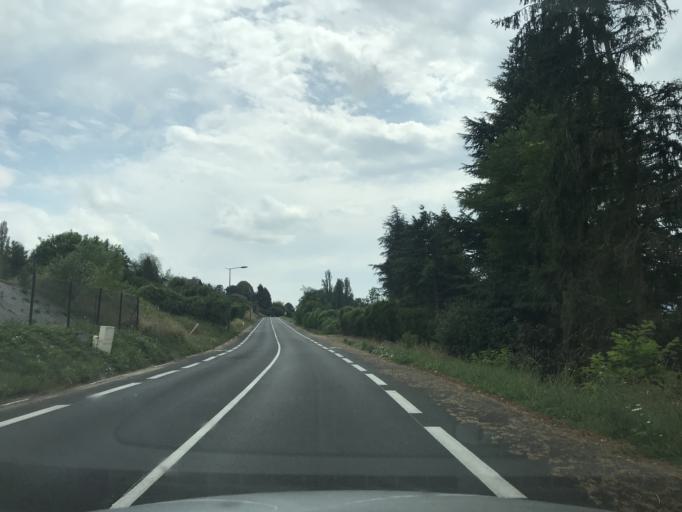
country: FR
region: Rhone-Alpes
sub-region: Departement de la Savoie
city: Brison-Saint-Innocent
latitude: 45.7293
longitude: 5.8807
